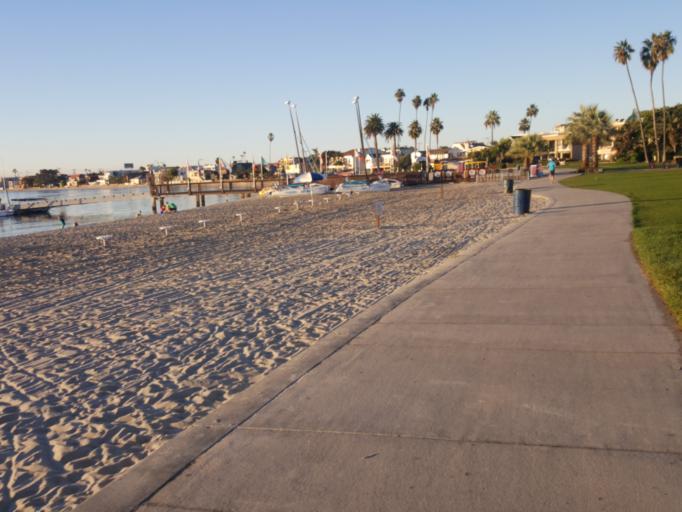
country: US
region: California
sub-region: San Diego County
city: La Jolla
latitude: 32.7899
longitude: -117.2515
